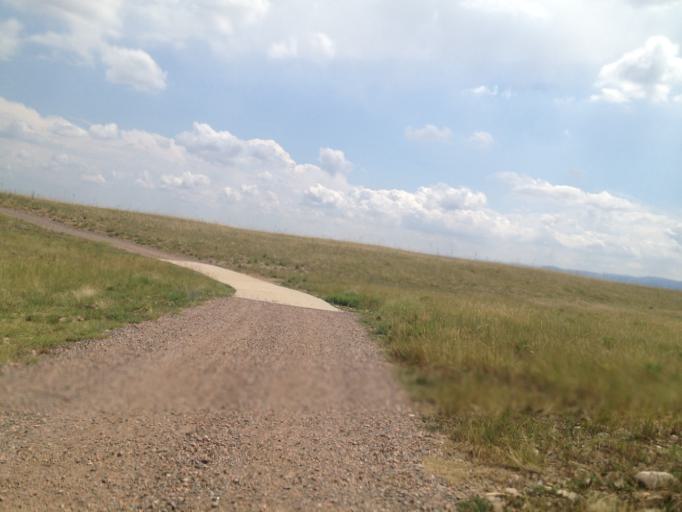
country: US
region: Colorado
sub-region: Boulder County
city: Superior
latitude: 39.9347
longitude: -105.1761
